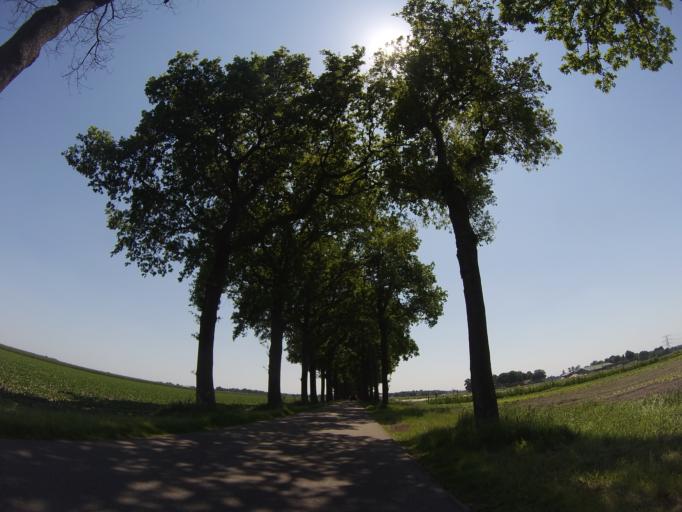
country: NL
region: Drenthe
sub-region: Gemeente Coevorden
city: Sleen
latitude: 52.7401
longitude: 6.8479
